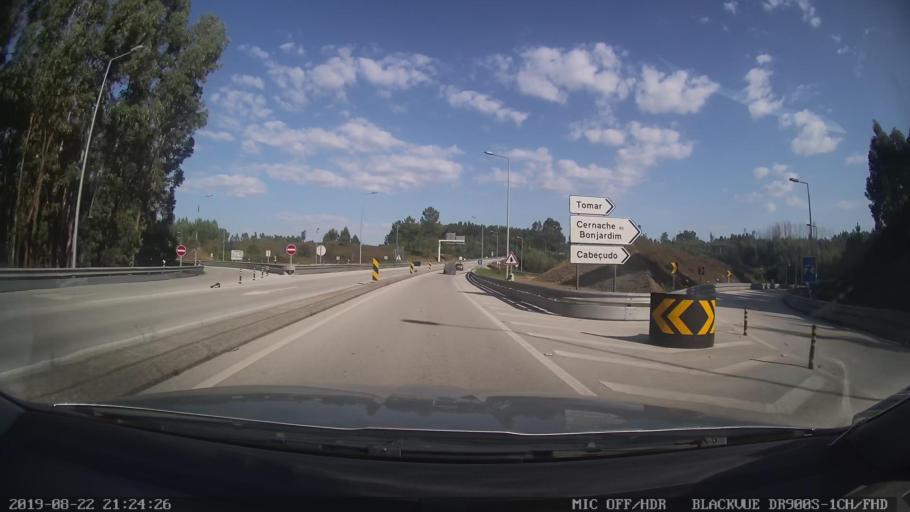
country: PT
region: Castelo Branco
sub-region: Serta
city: Serta
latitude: 39.8411
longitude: -8.1225
